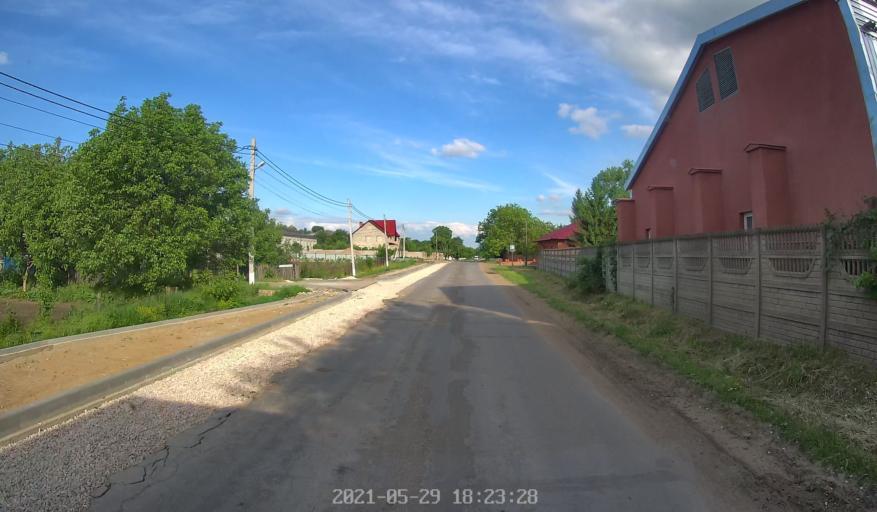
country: MD
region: Laloveni
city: Ialoveni
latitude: 46.8333
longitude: 28.8557
